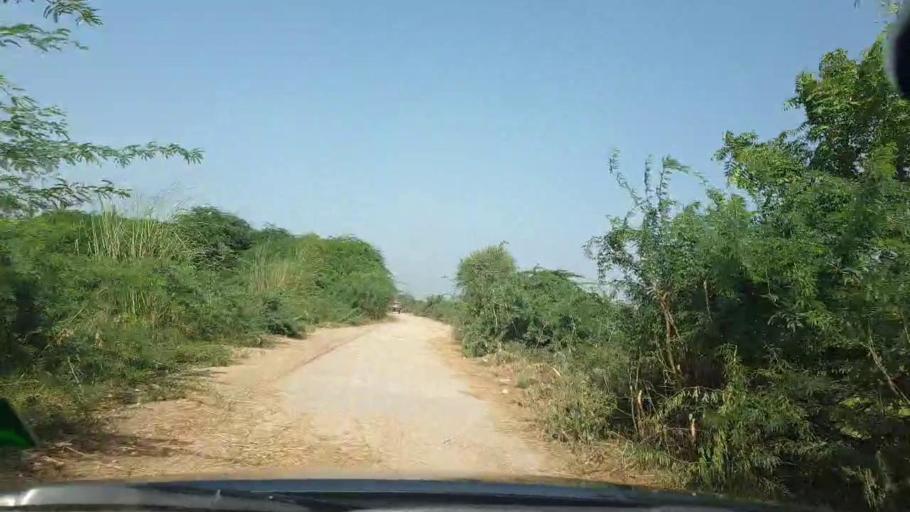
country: PK
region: Sindh
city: Tando Bago
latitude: 24.7722
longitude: 68.9543
